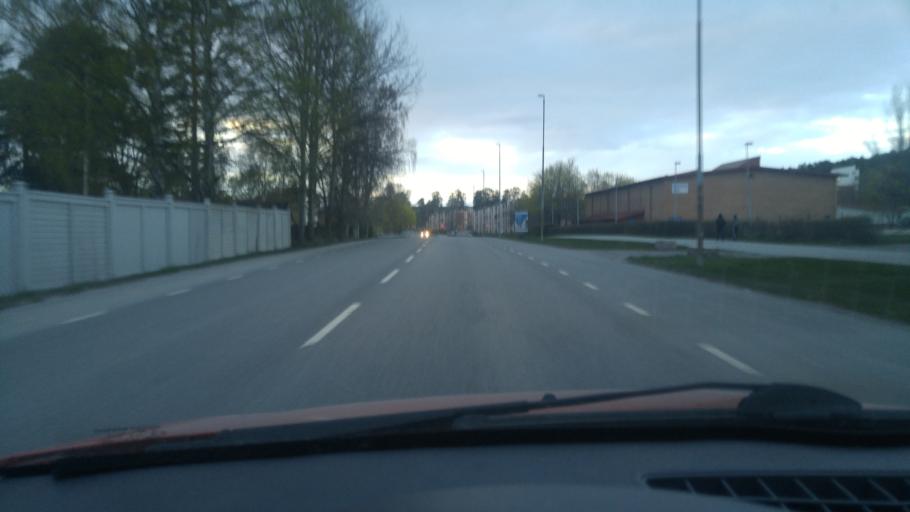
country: SE
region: Stockholm
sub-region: Upplands Vasby Kommun
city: Upplands Vaesby
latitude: 59.5203
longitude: 17.9177
